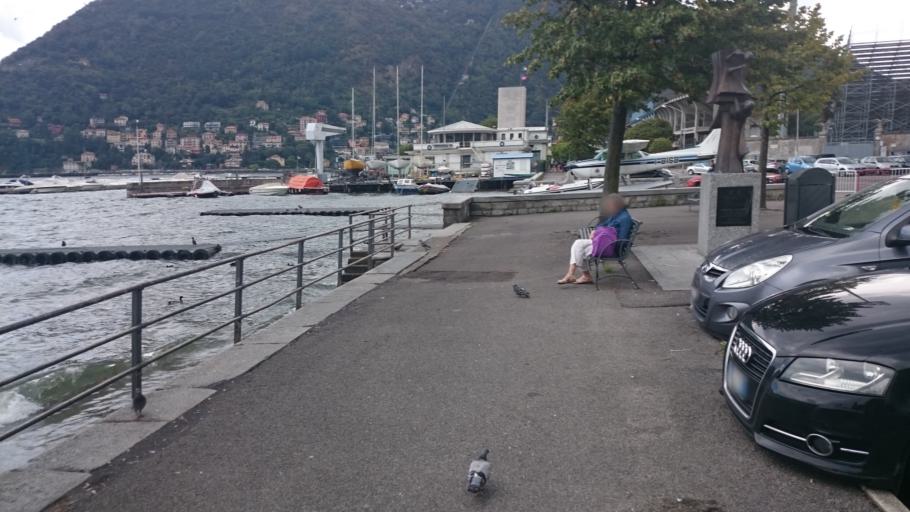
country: IT
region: Lombardy
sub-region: Provincia di Como
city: Como
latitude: 45.8143
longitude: 9.0700
